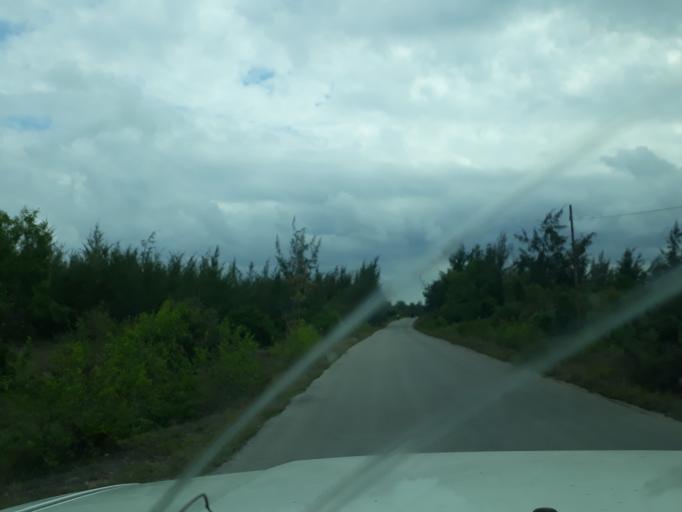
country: TZ
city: Kiwengwa
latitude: -6.0821
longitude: 39.4257
